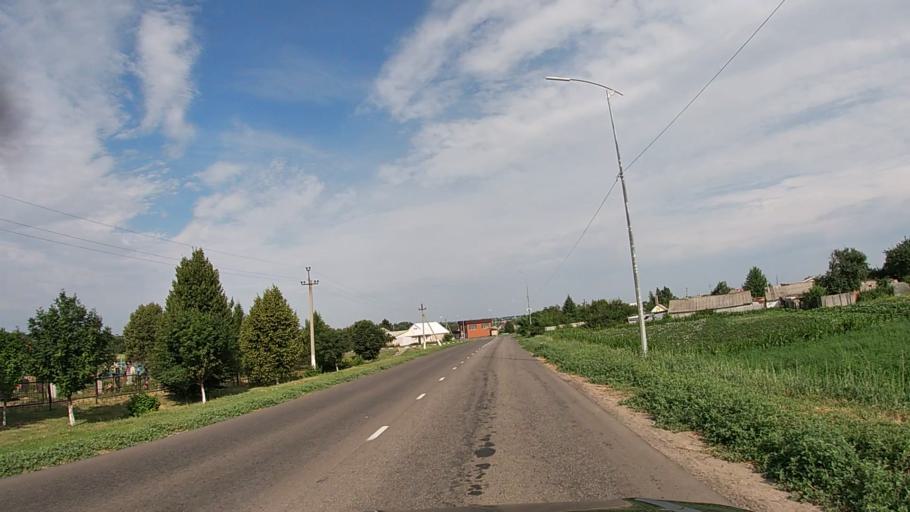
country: RU
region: Belgorod
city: Krasnaya Yaruga
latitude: 50.7990
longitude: 35.6784
